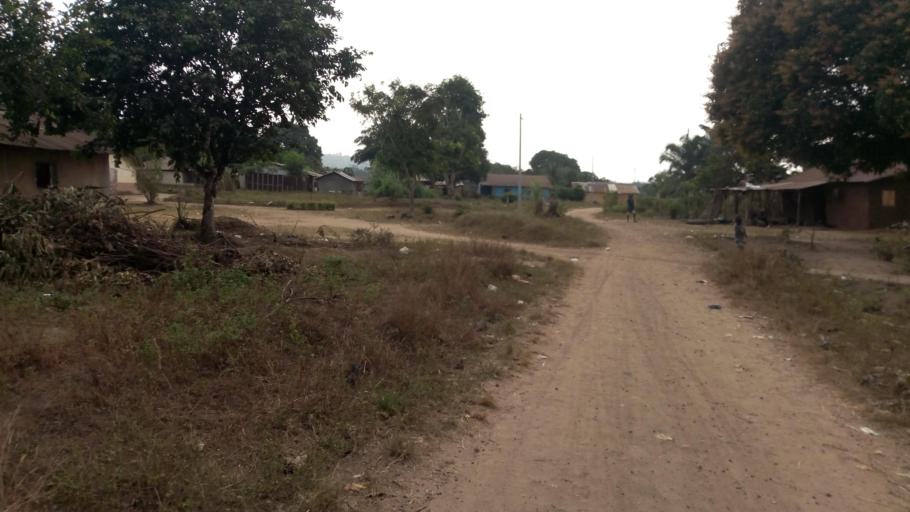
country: SL
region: Southern Province
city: Mogbwemo
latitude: 7.7633
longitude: -12.3126
